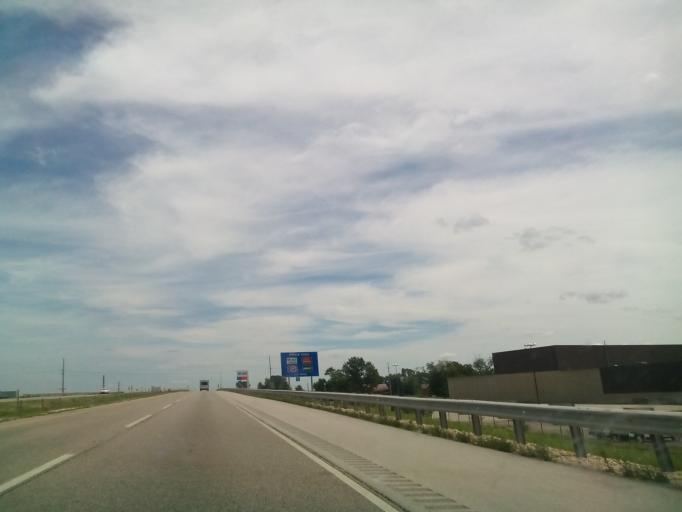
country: US
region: Illinois
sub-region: DeKalb County
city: DeKalb
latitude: 41.9032
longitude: -88.7572
